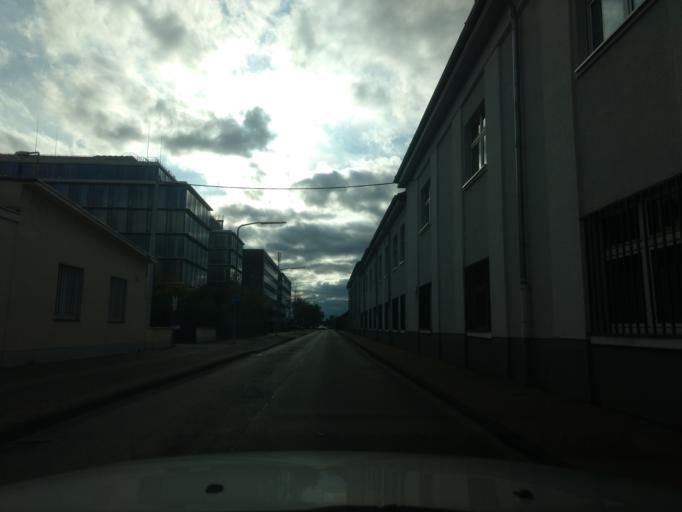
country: DE
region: North Rhine-Westphalia
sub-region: Regierungsbezirk Dusseldorf
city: Meerbusch
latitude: 51.2446
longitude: 6.7165
